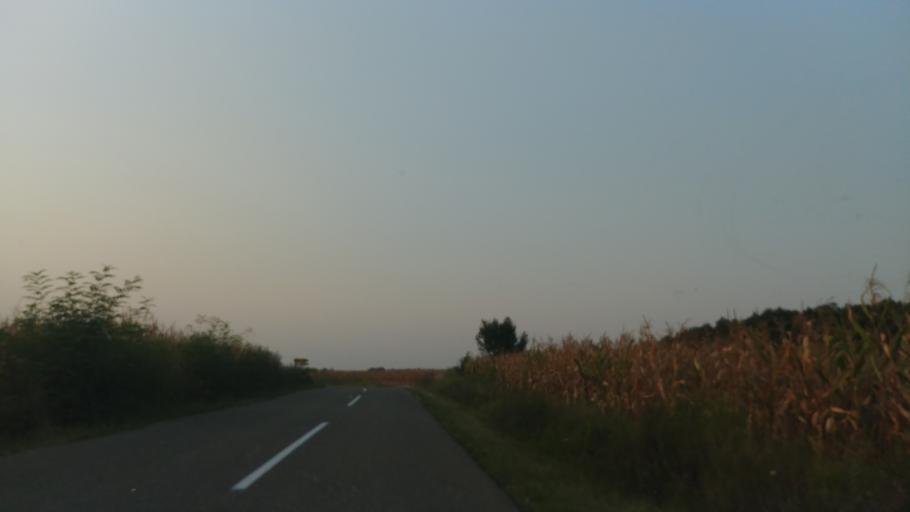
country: BA
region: Republika Srpska
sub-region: Opstina Ugljevik
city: Ugljevik
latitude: 44.7401
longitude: 18.9945
